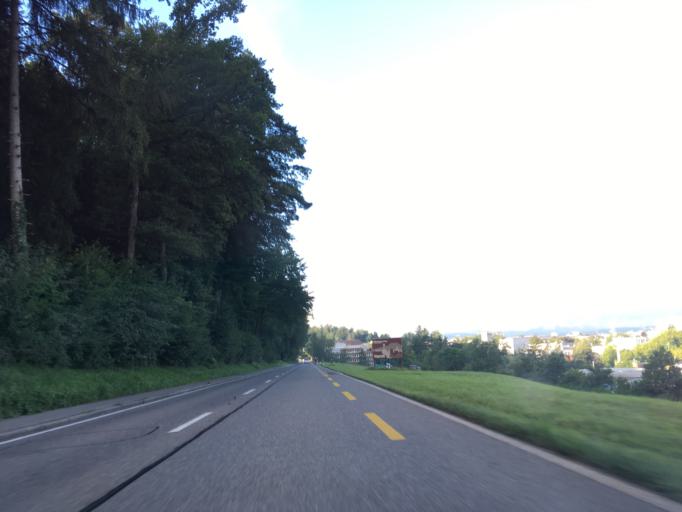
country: CH
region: Zug
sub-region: Zug
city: Baar
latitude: 47.2029
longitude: 8.5436
